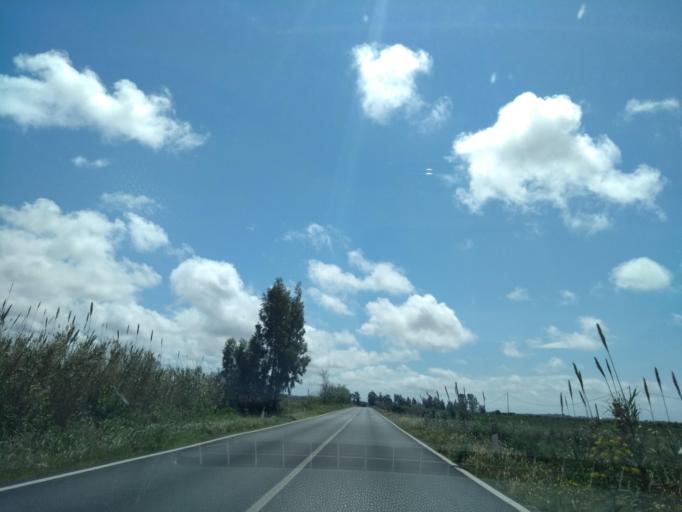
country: IT
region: Sicily
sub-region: Trapani
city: Rilievo
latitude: 37.8967
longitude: 12.5287
